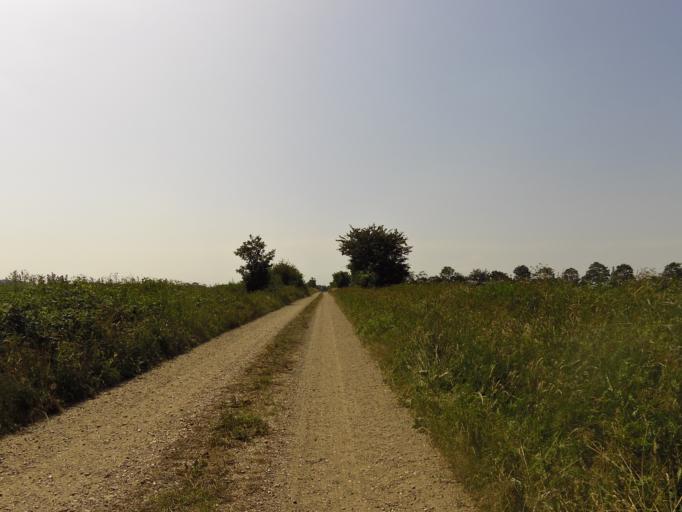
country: DK
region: South Denmark
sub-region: Aabenraa Kommune
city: Rodekro
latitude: 55.1429
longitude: 9.2300
